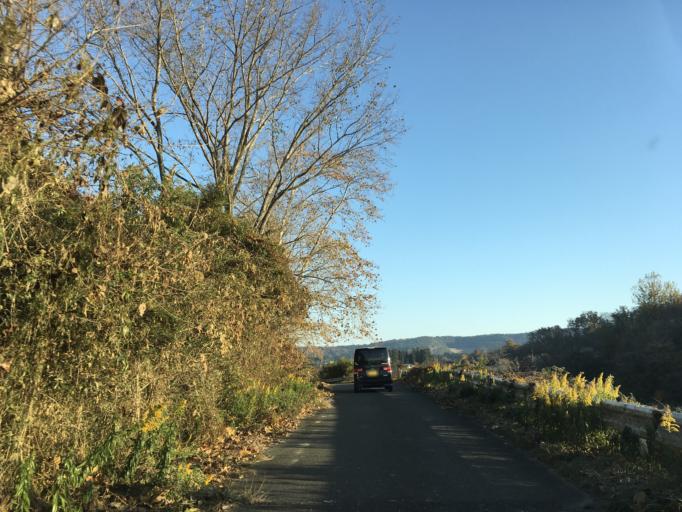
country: JP
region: Iwate
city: Ichinoseki
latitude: 38.7957
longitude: 141.2145
